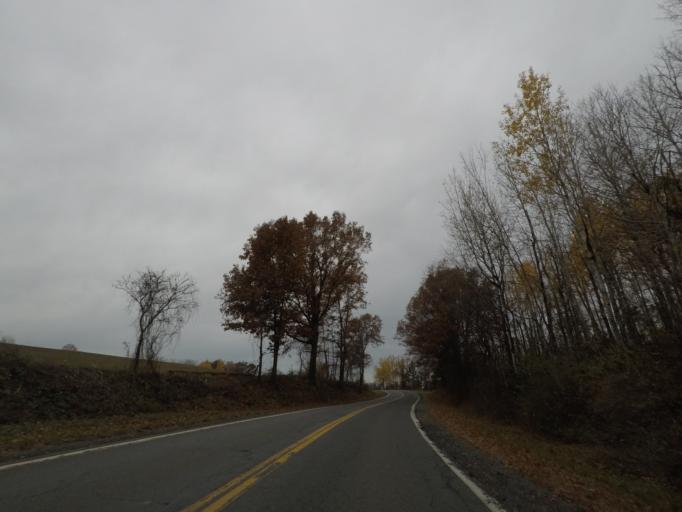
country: US
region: New York
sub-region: Saratoga County
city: Mechanicville
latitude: 42.8518
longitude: -73.7010
